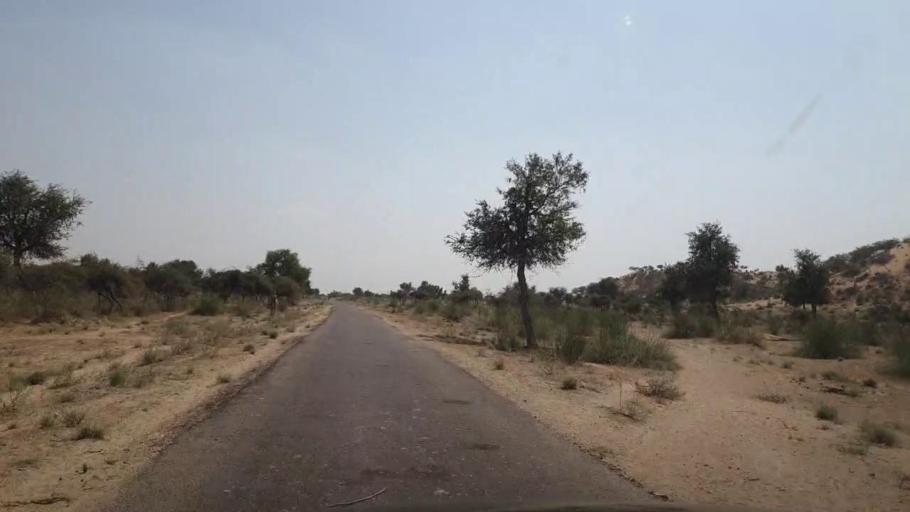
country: PK
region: Sindh
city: Islamkot
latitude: 25.1029
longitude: 70.7242
